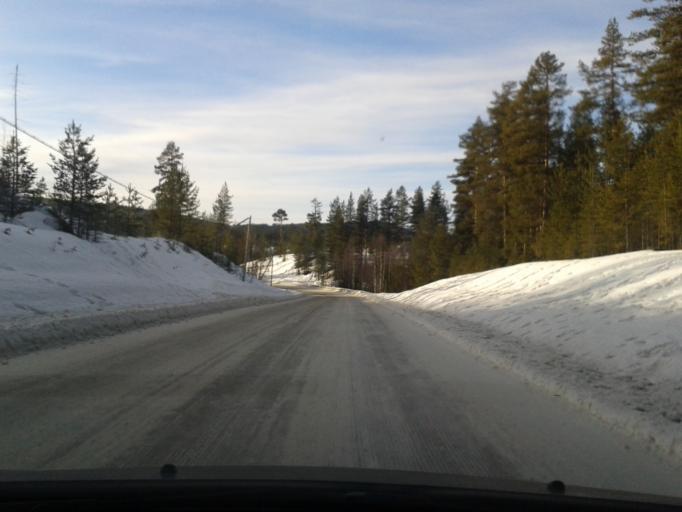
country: SE
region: Vaesternorrland
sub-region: OErnskoeldsviks Kommun
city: Bredbyn
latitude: 63.6751
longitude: 17.8128
